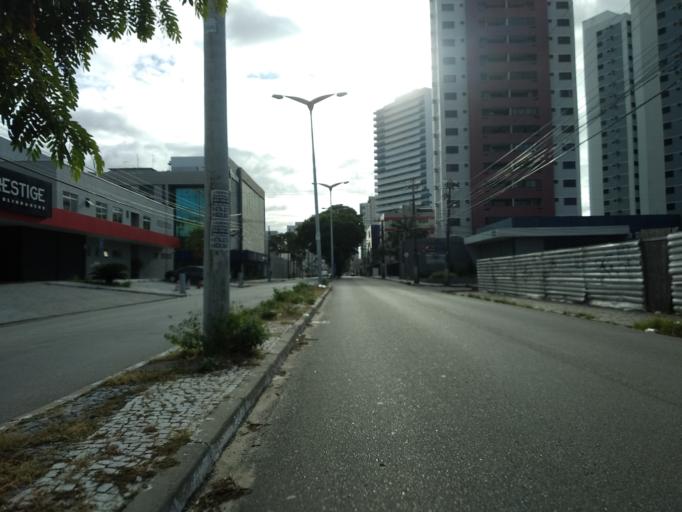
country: BR
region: Ceara
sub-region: Fortaleza
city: Fortaleza
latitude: -3.7354
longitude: -38.5187
